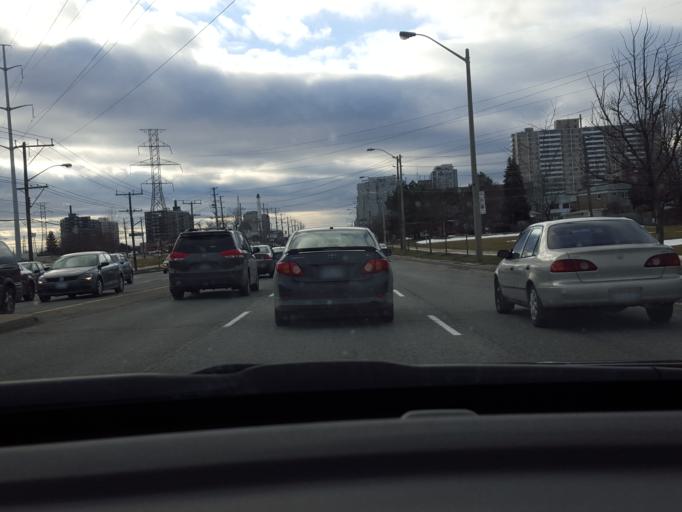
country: CA
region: Ontario
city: Scarborough
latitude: 43.7535
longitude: -79.2558
